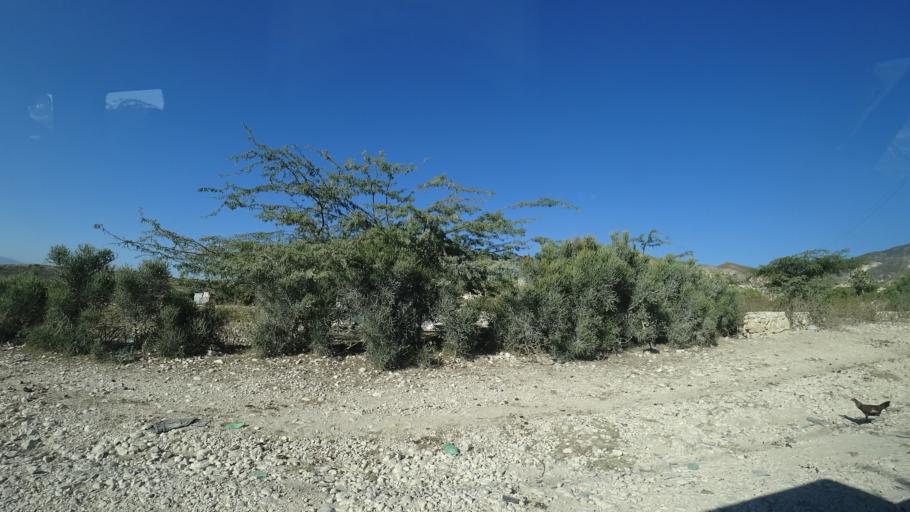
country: HT
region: Ouest
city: Croix des Bouquets
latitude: 18.6748
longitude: -72.2420
